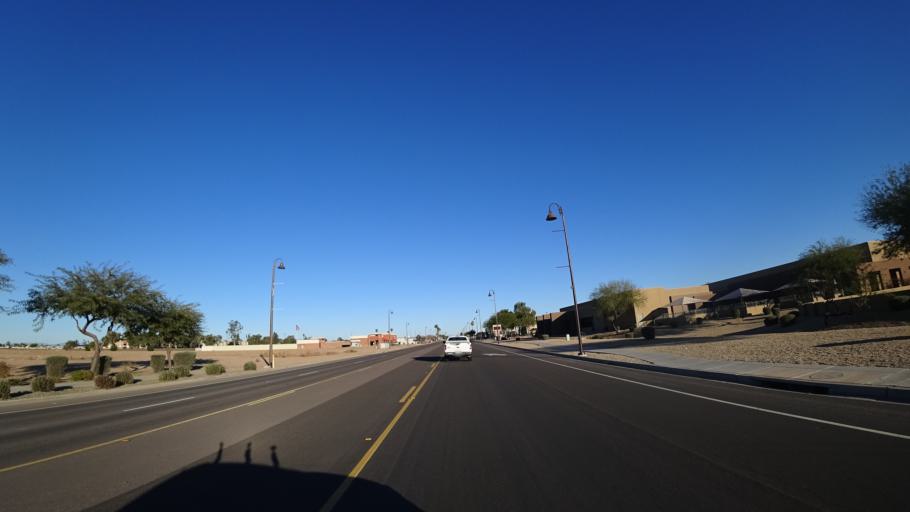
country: US
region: Arizona
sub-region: Maricopa County
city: Tolleson
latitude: 33.4502
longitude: -112.2704
